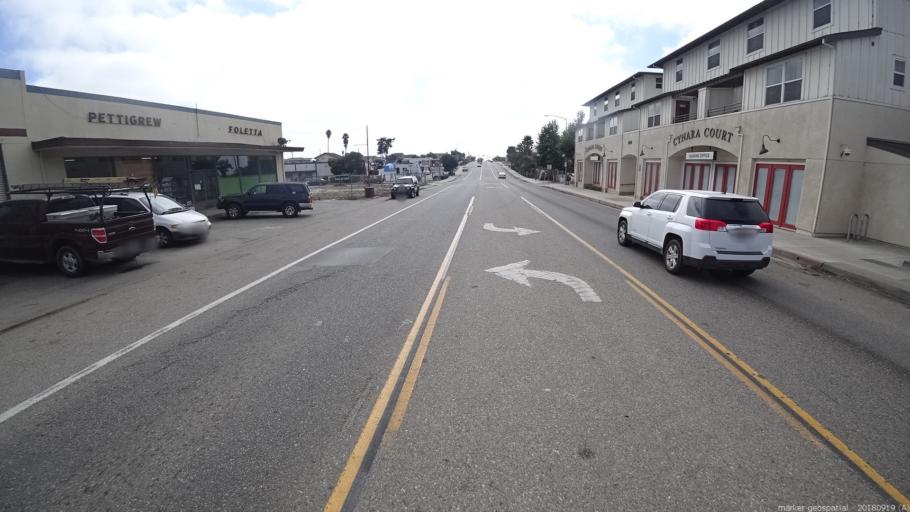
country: US
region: California
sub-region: Monterey County
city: Castroville
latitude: 36.7650
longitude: -121.7569
